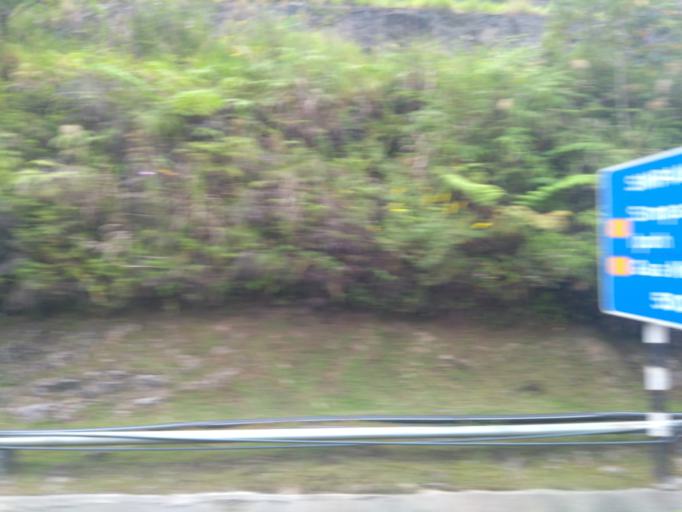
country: MY
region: Pahang
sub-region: Cameron Highlands
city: Tanah Rata
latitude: 4.5804
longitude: 101.4159
